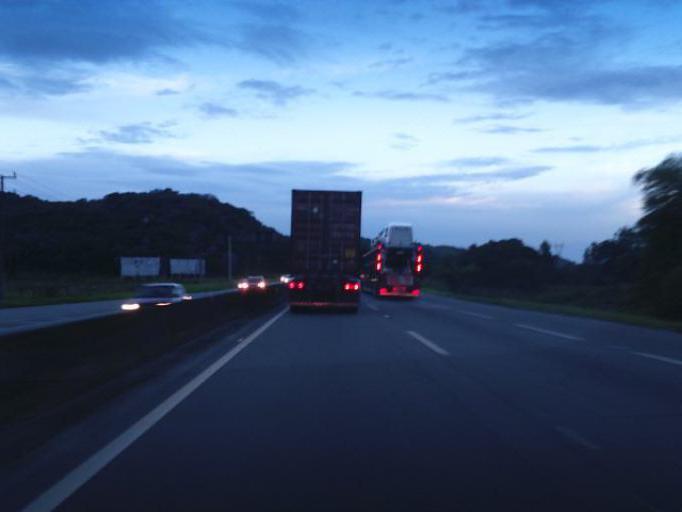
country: BR
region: Santa Catarina
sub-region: Joinville
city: Joinville
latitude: -26.2504
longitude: -48.9087
